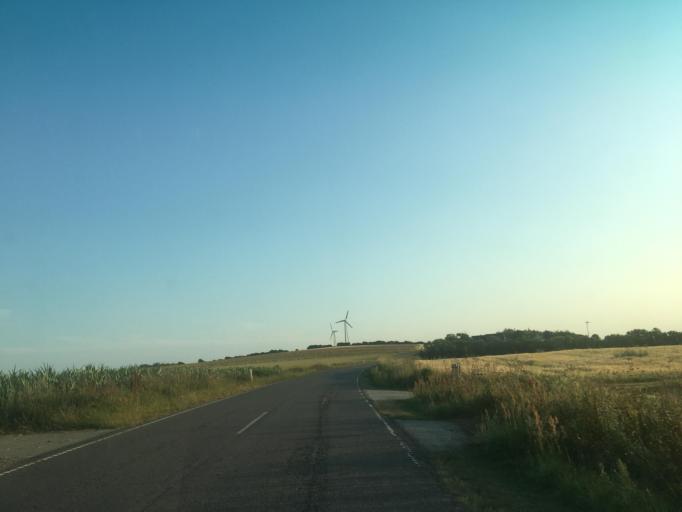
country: DK
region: North Denmark
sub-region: Thisted Kommune
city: Hurup
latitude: 56.8056
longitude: 8.3429
